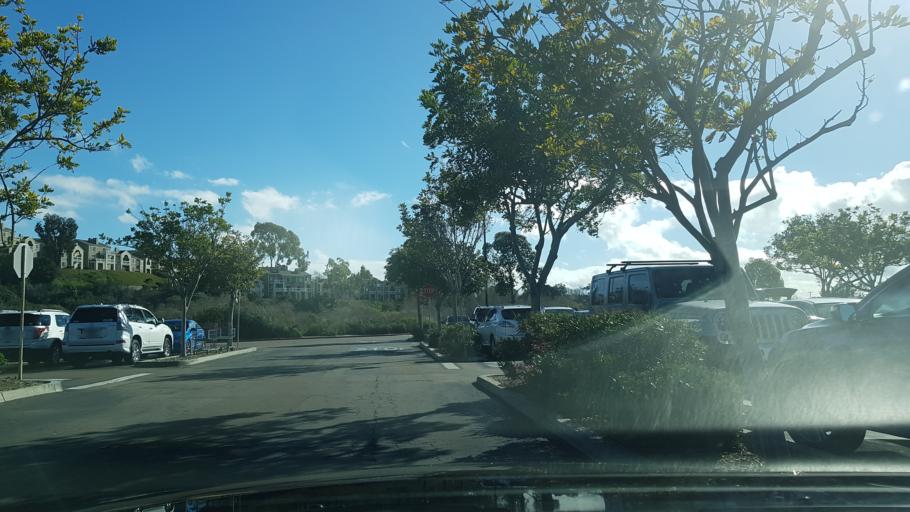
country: US
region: California
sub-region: San Diego County
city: Carlsbad
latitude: 33.1208
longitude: -117.3147
